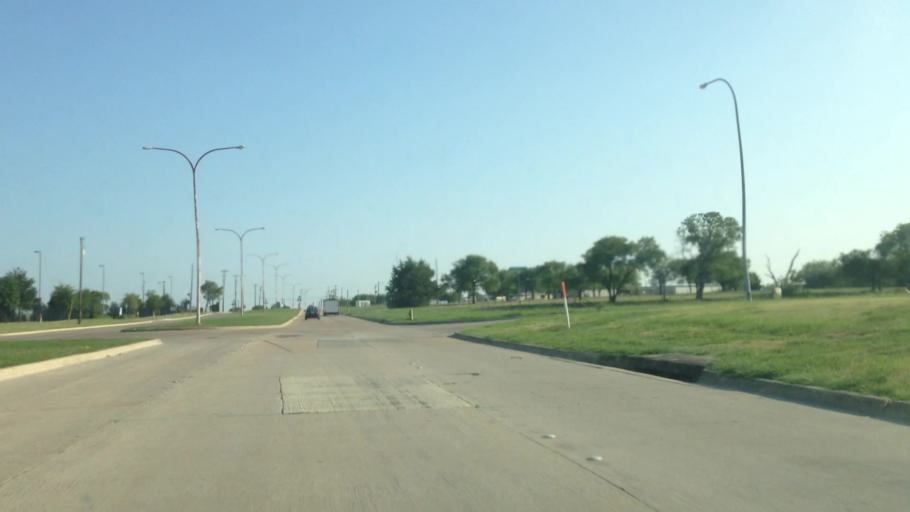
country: US
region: Texas
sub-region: Tarrant County
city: Haltom City
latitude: 32.8163
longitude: -97.3084
